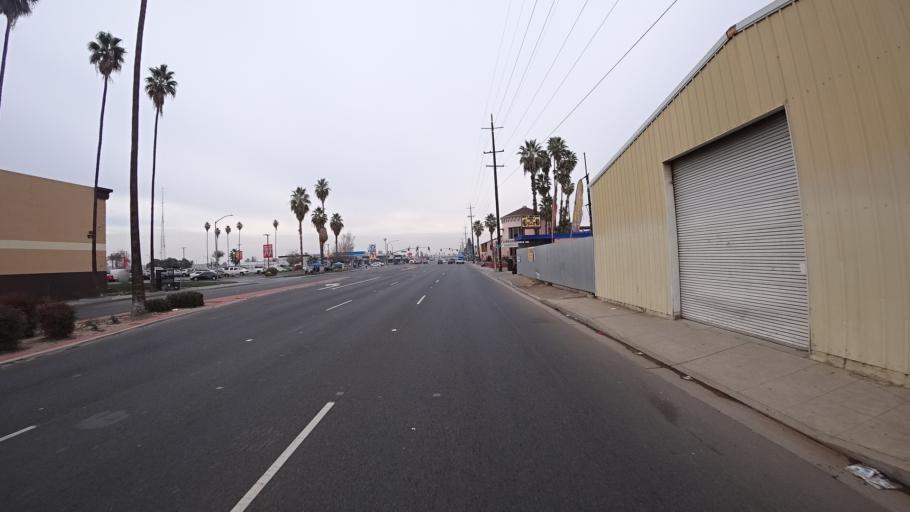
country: US
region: California
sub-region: Kern County
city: Bakersfield
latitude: 35.3669
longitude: -119.0028
